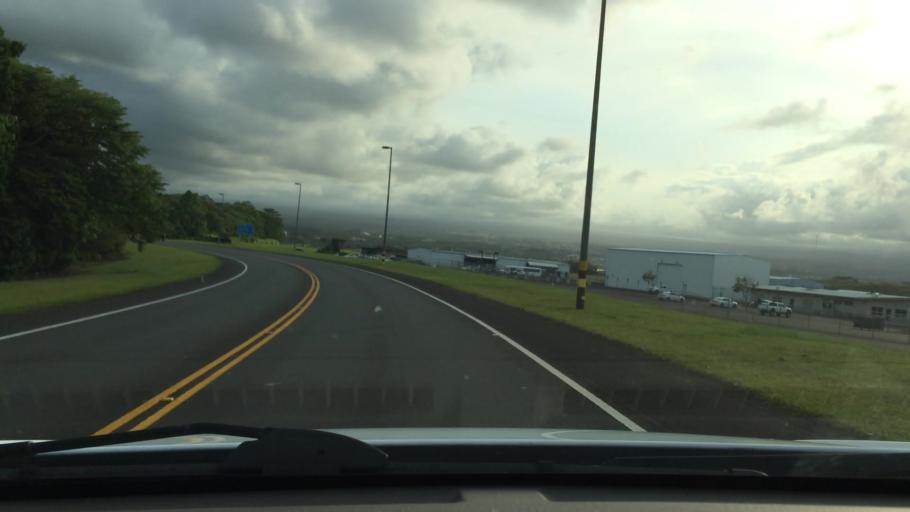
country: US
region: Hawaii
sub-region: Hawaii County
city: Hilo
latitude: 19.7158
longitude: -155.0545
